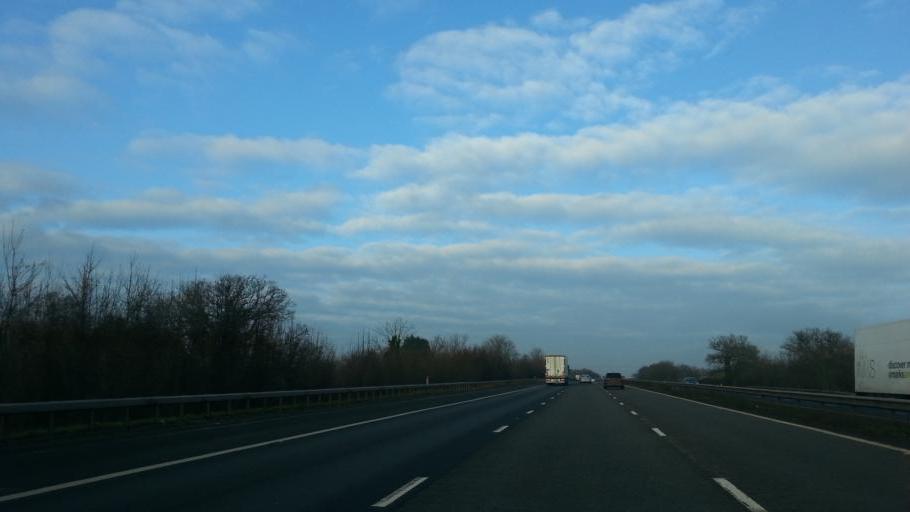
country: GB
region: England
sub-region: Gloucestershire
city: Dursley
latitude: 51.6832
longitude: -2.4008
